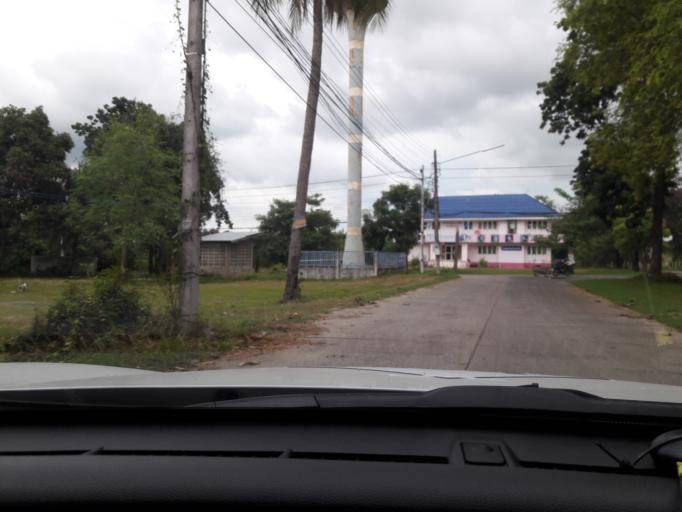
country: TH
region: Nakhon Sawan
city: Tak Fa
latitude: 15.3513
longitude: 100.4945
